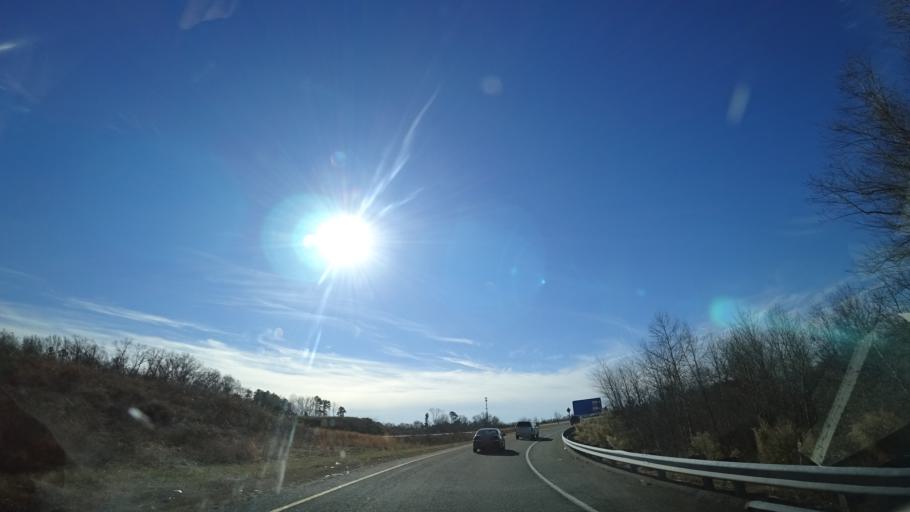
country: US
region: Virginia
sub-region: Henrico County
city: Glen Allen
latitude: 37.6896
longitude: -77.4492
